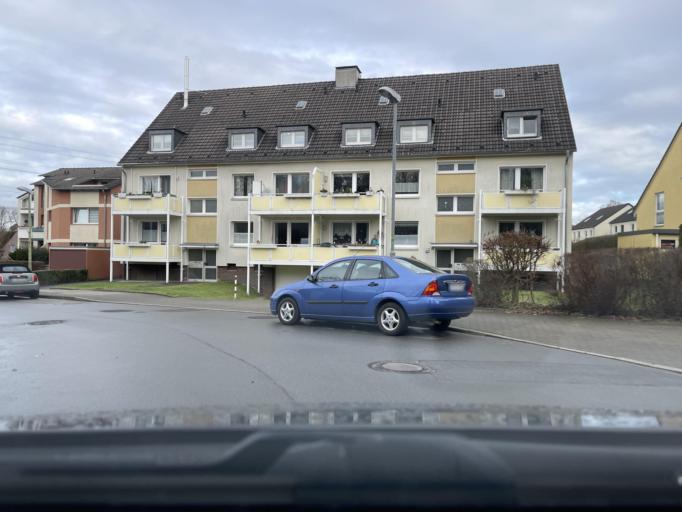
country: DE
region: North Rhine-Westphalia
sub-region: Regierungsbezirk Dusseldorf
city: Essen
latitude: 51.4558
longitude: 6.9579
